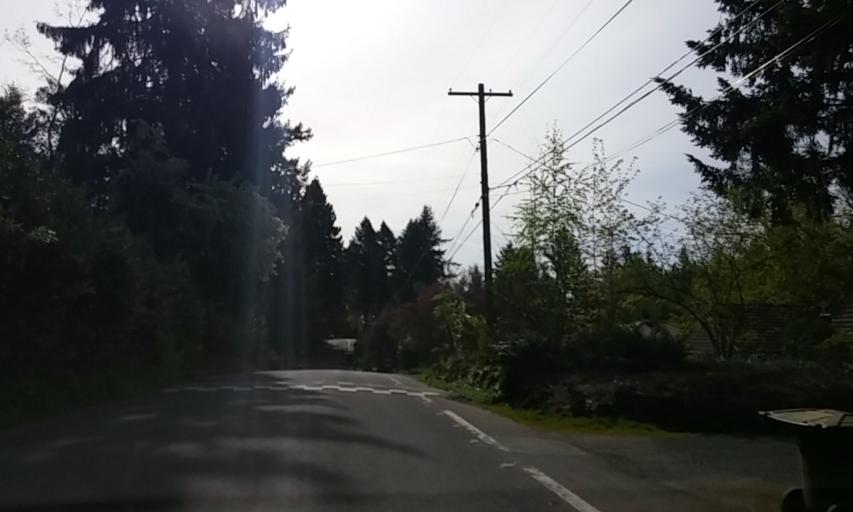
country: US
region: Oregon
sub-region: Washington County
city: West Slope
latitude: 45.5036
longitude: -122.7578
